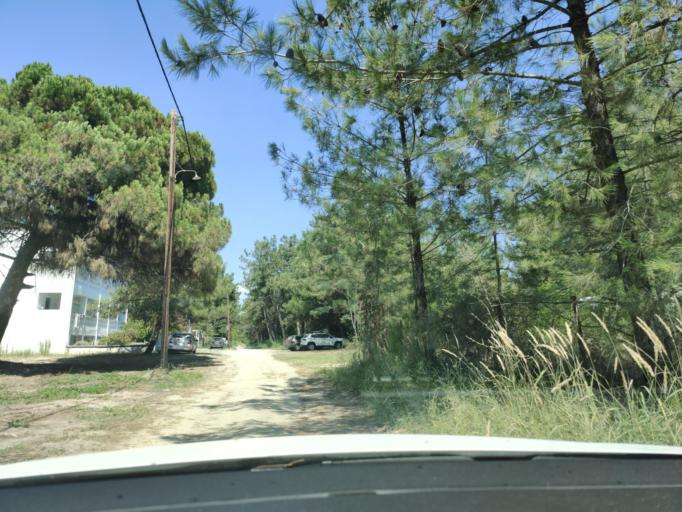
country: GR
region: East Macedonia and Thrace
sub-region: Nomos Kavalas
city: Prinos
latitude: 40.7582
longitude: 24.5628
